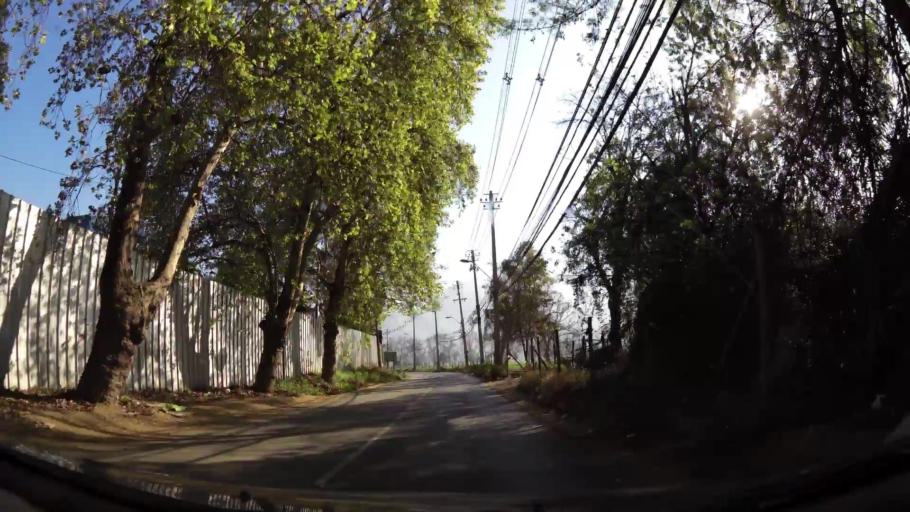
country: CL
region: Santiago Metropolitan
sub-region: Provincia de Santiago
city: Santiago
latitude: -33.3710
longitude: -70.6603
